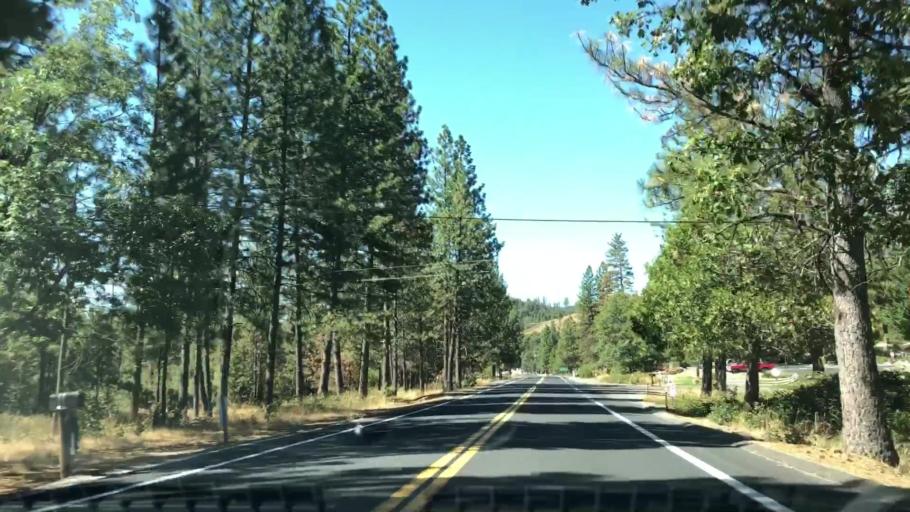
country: US
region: California
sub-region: Tuolumne County
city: Tuolumne City
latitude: 37.8172
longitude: -120.0583
